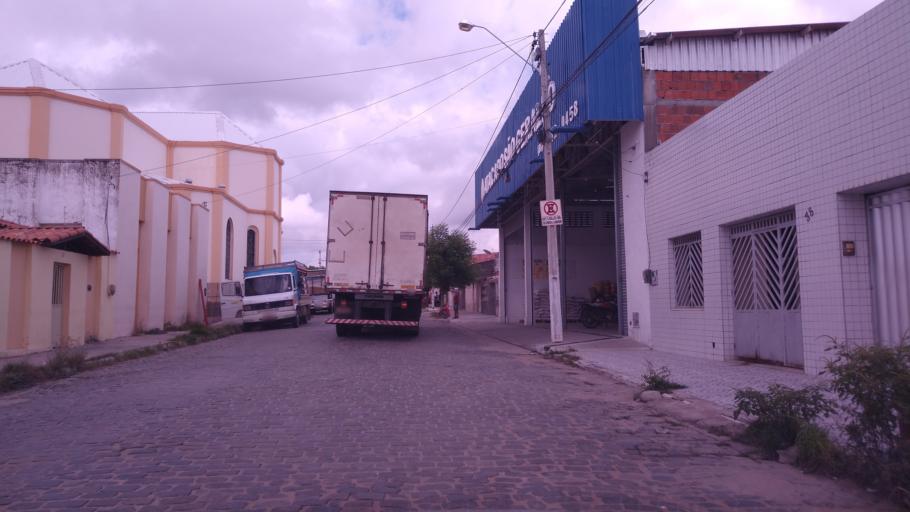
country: BR
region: Ceara
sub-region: Quixada
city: Quixada
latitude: -4.9668
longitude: -39.0164
